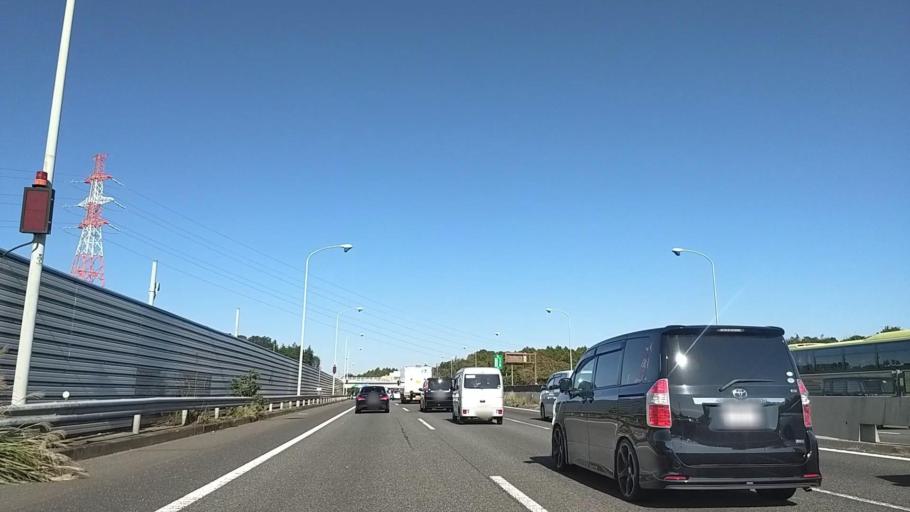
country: JP
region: Kanagawa
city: Minami-rinkan
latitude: 35.4876
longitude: 139.5076
